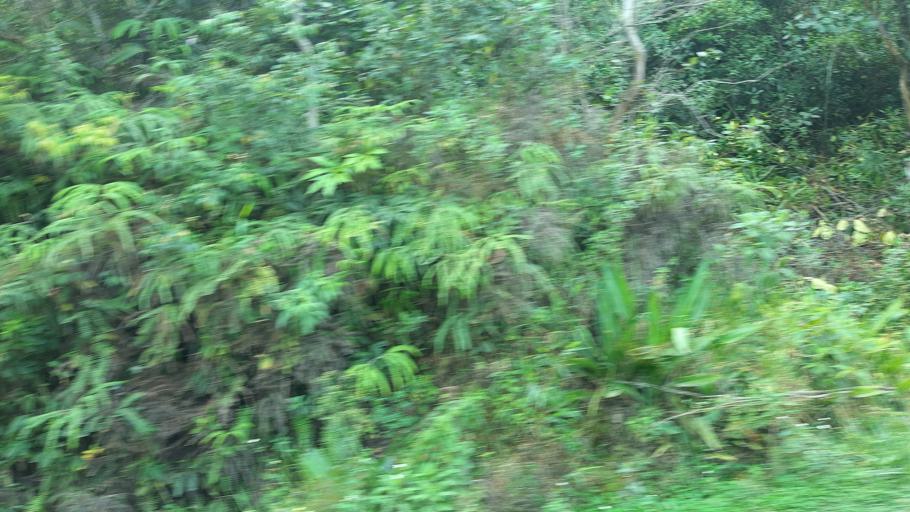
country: CO
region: Boyaca
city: Santa Sofia
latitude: 5.7845
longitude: -73.6036
